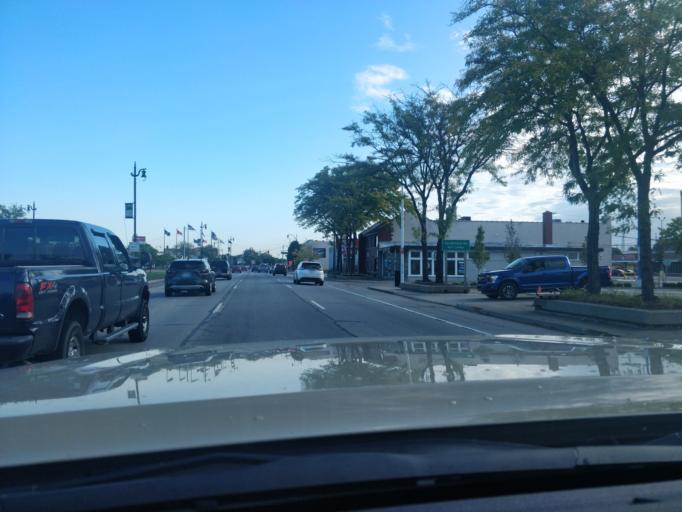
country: US
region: Michigan
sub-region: Wayne County
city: Lincoln Park
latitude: 42.2487
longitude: -83.1777
